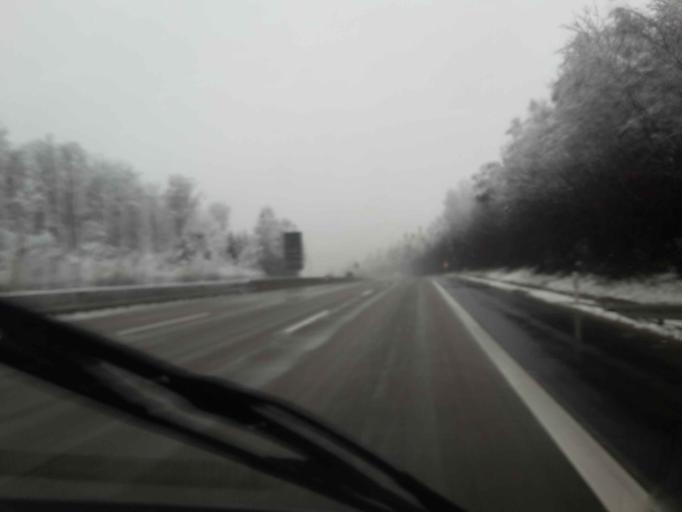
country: DE
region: Hesse
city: Schwarzenborn
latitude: 50.9518
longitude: 9.5094
